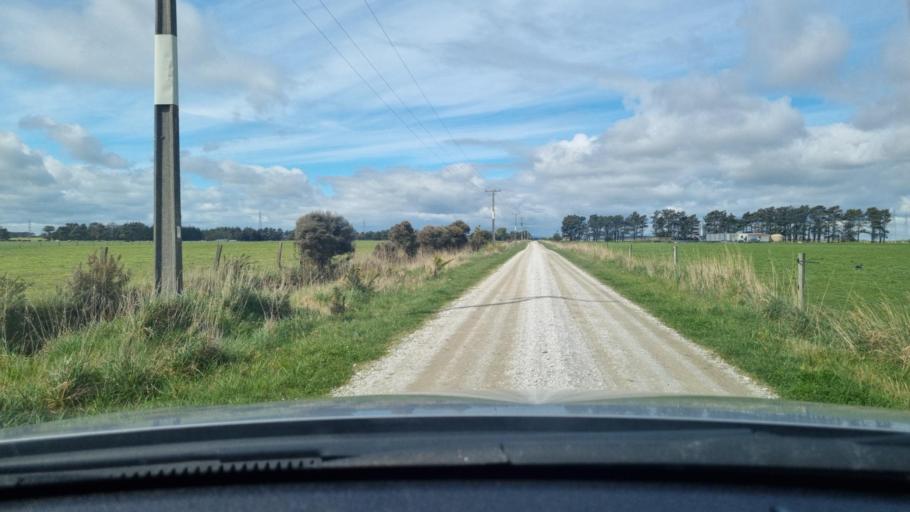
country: NZ
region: Southland
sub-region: Invercargill City
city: Invercargill
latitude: -46.4768
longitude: 168.4216
